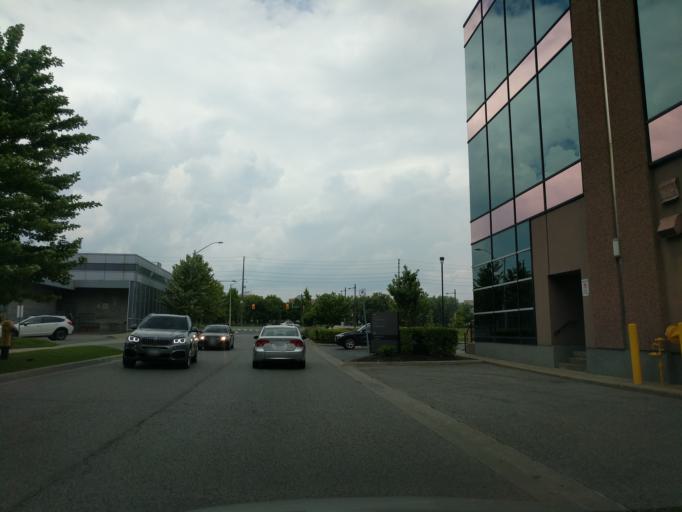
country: CA
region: Ontario
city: Markham
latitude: 43.8536
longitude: -79.3366
